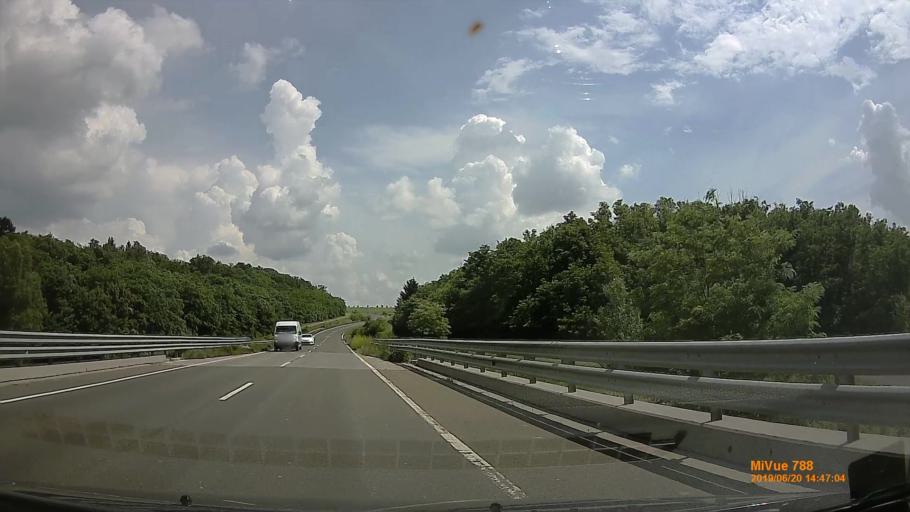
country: HU
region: Baranya
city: Kozarmisleny
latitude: 46.0267
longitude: 18.2782
